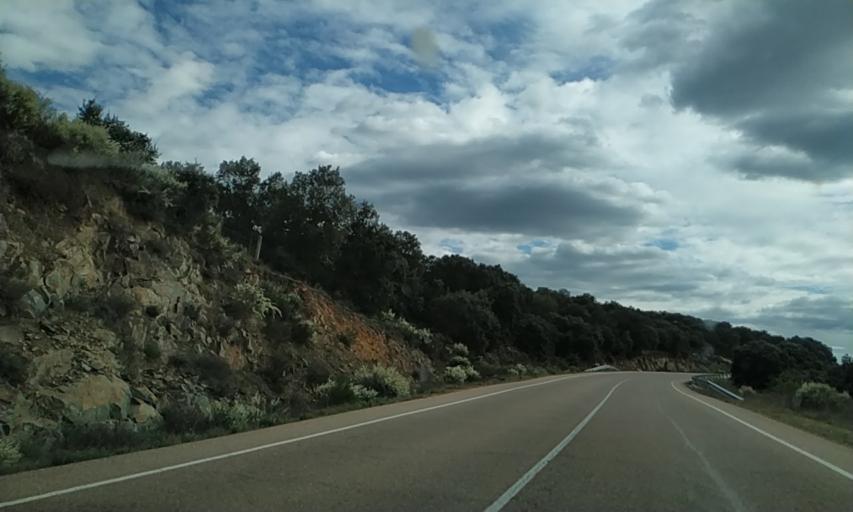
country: ES
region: Castille and Leon
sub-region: Provincia de Salamanca
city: Pastores
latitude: 40.5073
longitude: -6.5738
